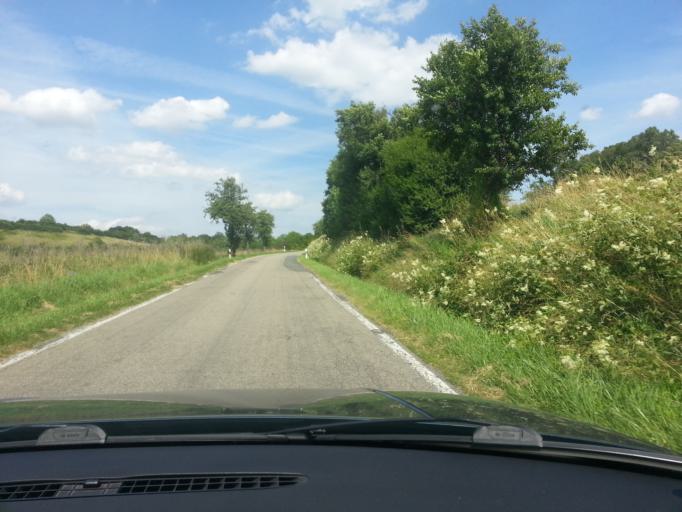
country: DE
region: Rheinland-Pfalz
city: Hornbach
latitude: 49.1730
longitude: 7.3201
